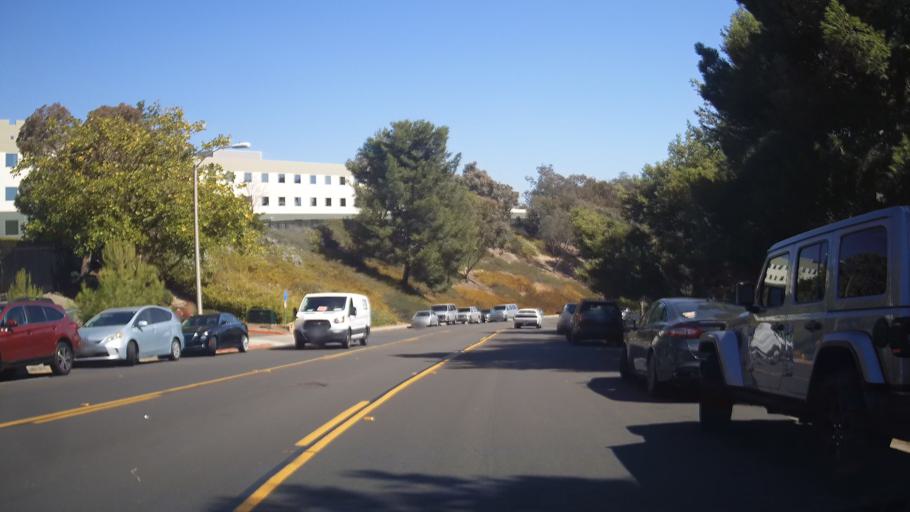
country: US
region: California
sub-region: San Diego County
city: San Diego
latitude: 32.8234
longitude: -117.1245
